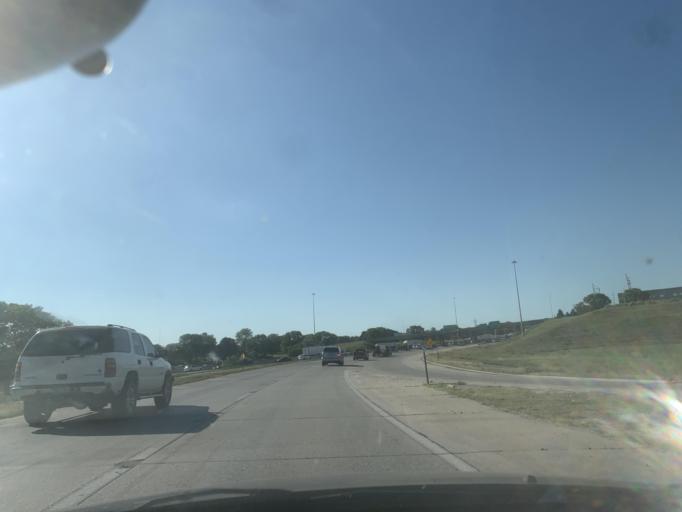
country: US
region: Nebraska
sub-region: Douglas County
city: Ralston
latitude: 41.2136
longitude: -96.0892
